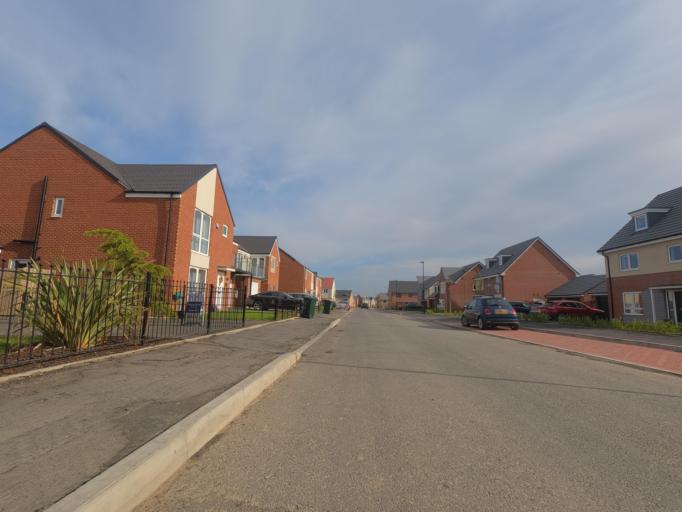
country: GB
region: England
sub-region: Newcastle upon Tyne
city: Hazlerigg
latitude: 55.0310
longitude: -1.6617
